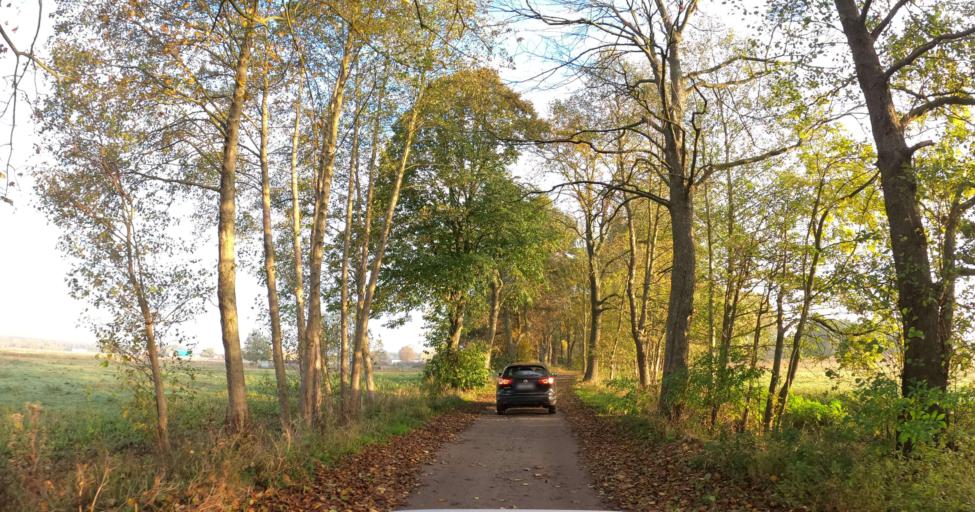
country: PL
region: West Pomeranian Voivodeship
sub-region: Powiat goleniowski
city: Goleniow
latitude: 53.5715
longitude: 14.7619
